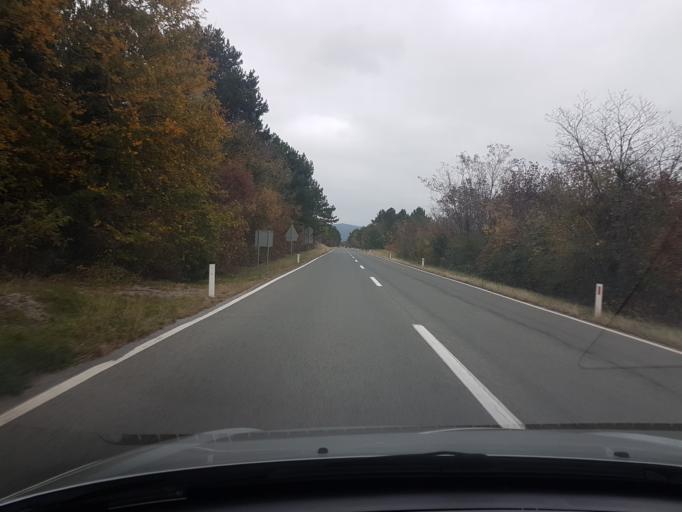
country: SI
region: Sezana
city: Sezana
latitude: 45.7228
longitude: 13.9022
